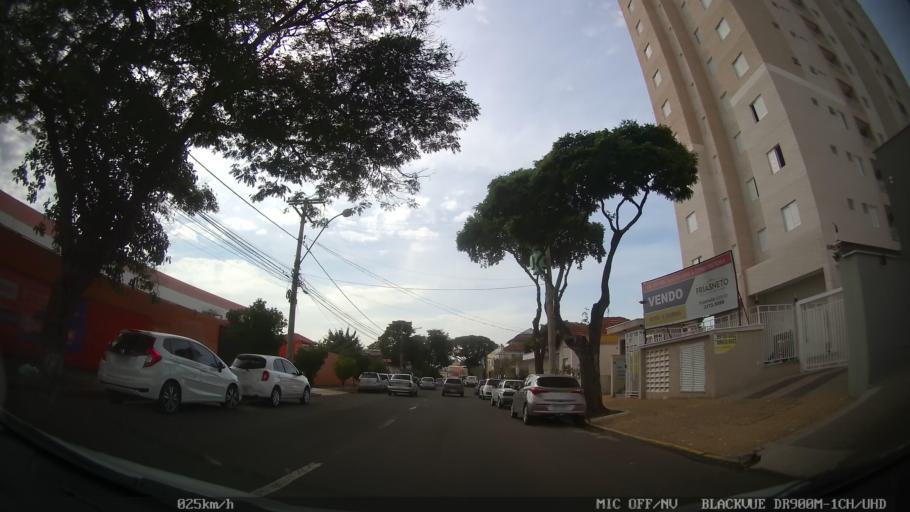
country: BR
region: Sao Paulo
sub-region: Piracicaba
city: Piracicaba
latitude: -22.7110
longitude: -47.6543
